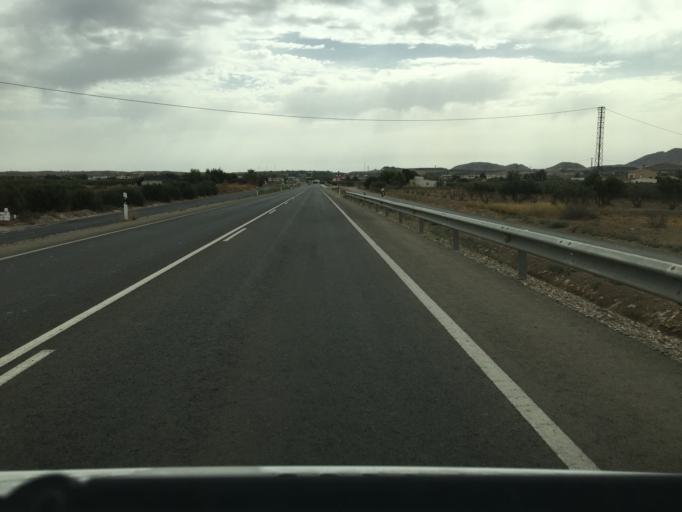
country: ES
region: Andalusia
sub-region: Provincia de Almeria
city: Huercal-Overa
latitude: 37.4145
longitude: -1.8998
